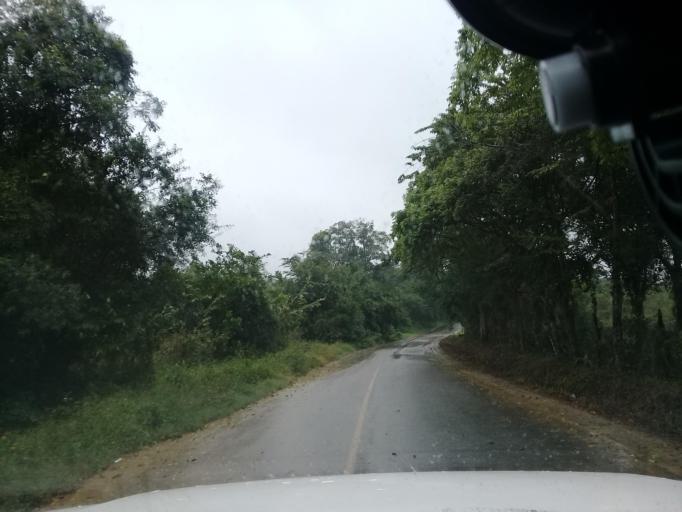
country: MX
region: Hidalgo
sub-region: Huejutla de Reyes
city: Huejutla de Reyes
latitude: 21.1786
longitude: -98.4376
